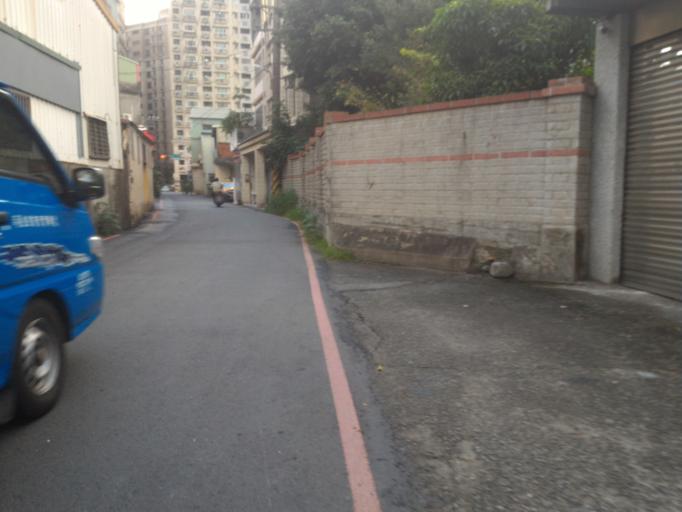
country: TW
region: Taiwan
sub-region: Taoyuan
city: Taoyuan
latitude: 24.9426
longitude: 121.3801
